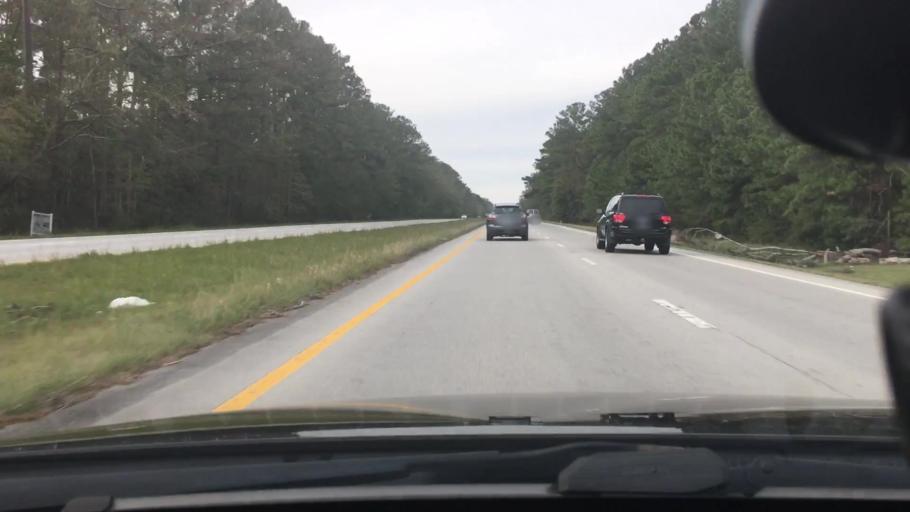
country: US
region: North Carolina
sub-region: Craven County
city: Fairfield Harbour
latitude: 35.0174
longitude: -76.9959
